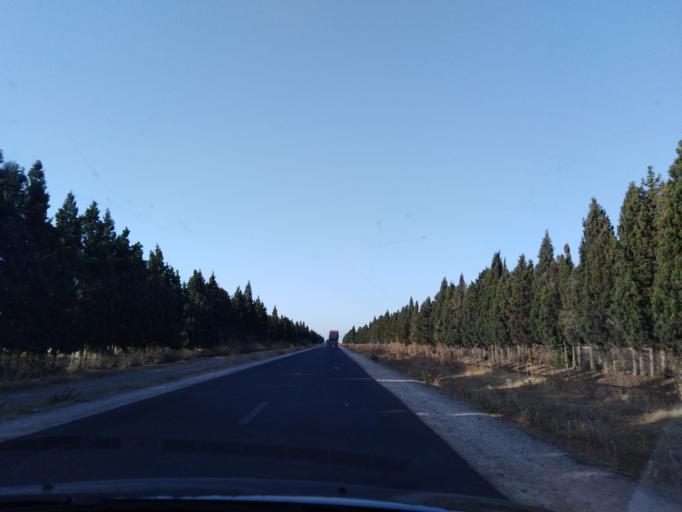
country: MA
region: Doukkala-Abda
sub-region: Safi
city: Safi
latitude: 32.4998
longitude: -8.9257
